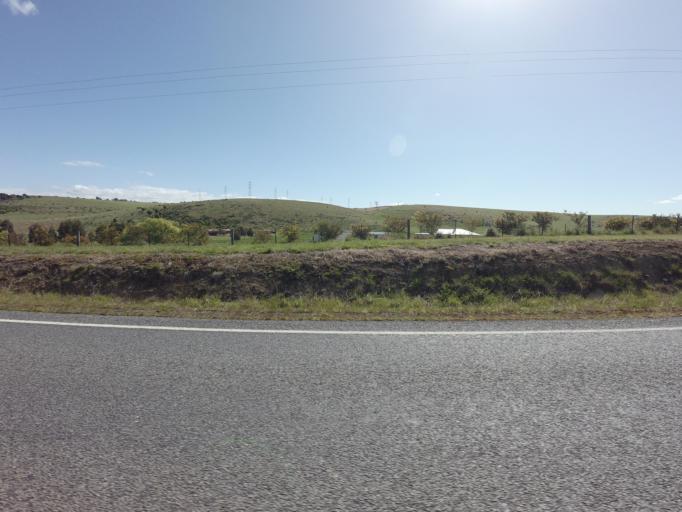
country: AU
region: Tasmania
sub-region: Derwent Valley
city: New Norfolk
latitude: -42.6604
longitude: 146.9354
